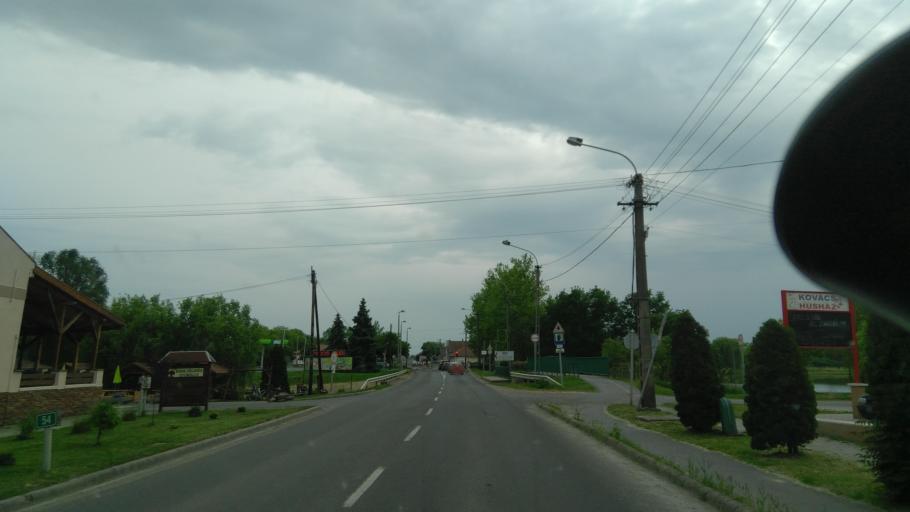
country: HU
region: Bekes
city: Sarkad
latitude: 46.7403
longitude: 21.3760
